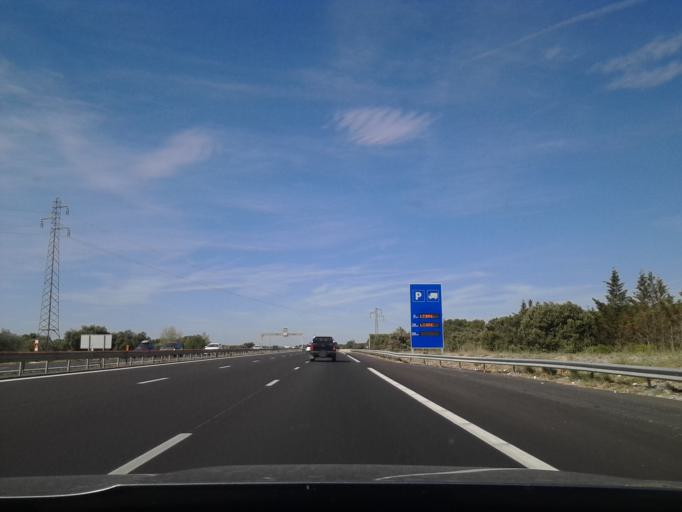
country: FR
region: Languedoc-Roussillon
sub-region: Departement de l'Herault
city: Poussan
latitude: 43.4751
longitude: 3.6500
